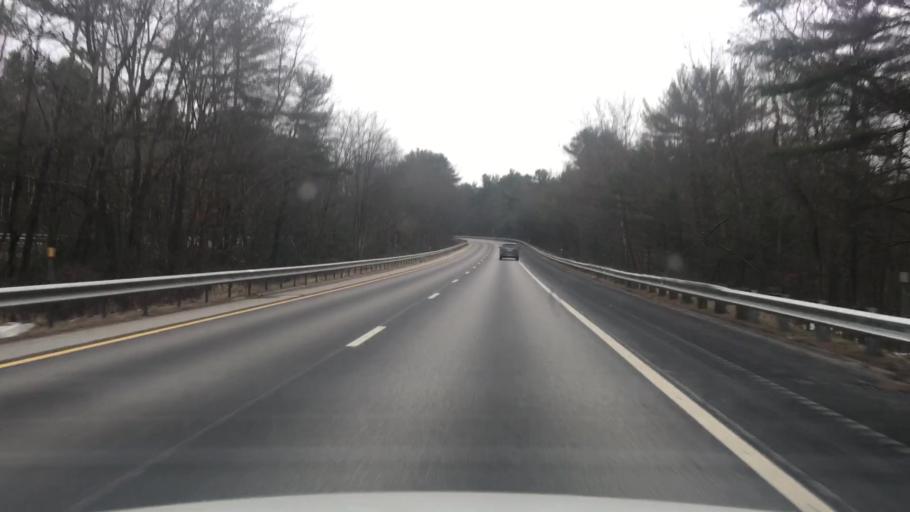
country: US
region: New Hampshire
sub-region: Merrimack County
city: Hopkinton
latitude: 43.1766
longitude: -71.6201
